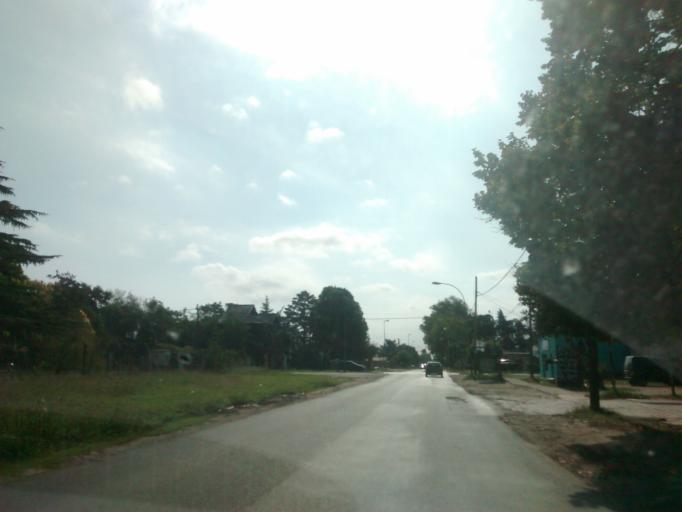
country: AR
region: Buenos Aires
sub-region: Partido de La Plata
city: La Plata
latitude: -34.9582
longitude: -57.8923
